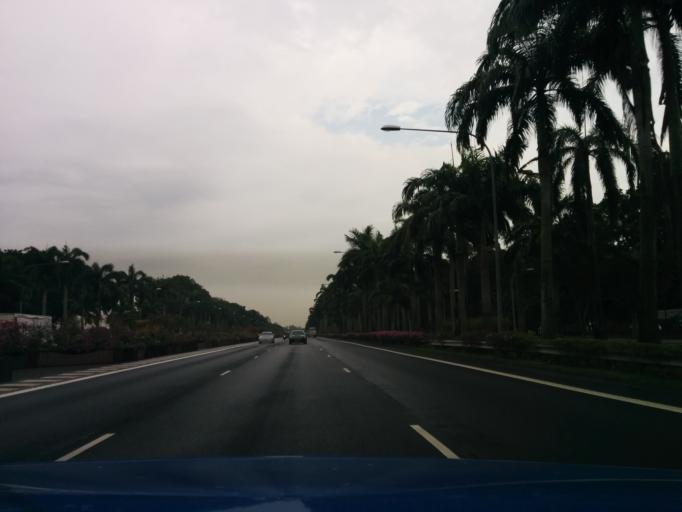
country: SG
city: Singapore
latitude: 1.3132
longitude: 103.9544
